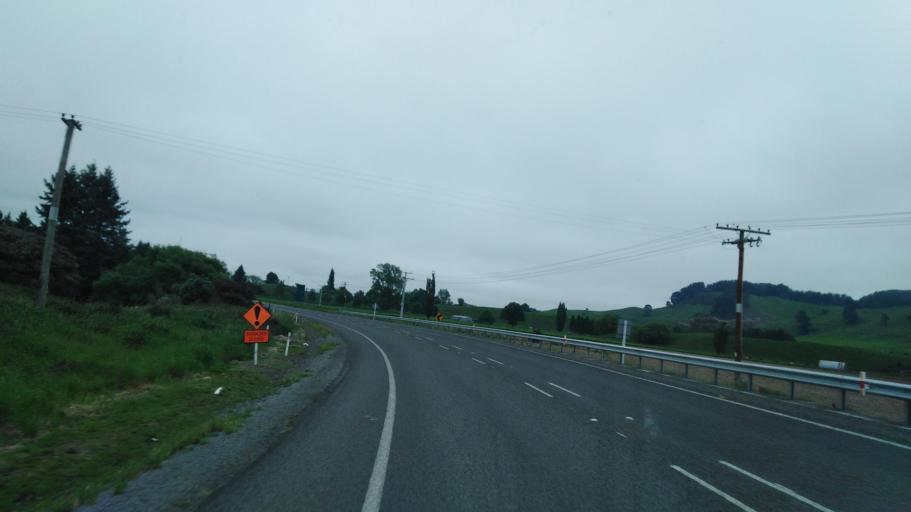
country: NZ
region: Bay of Plenty
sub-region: Rotorua District
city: Rotorua
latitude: -38.3654
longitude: 176.3535
